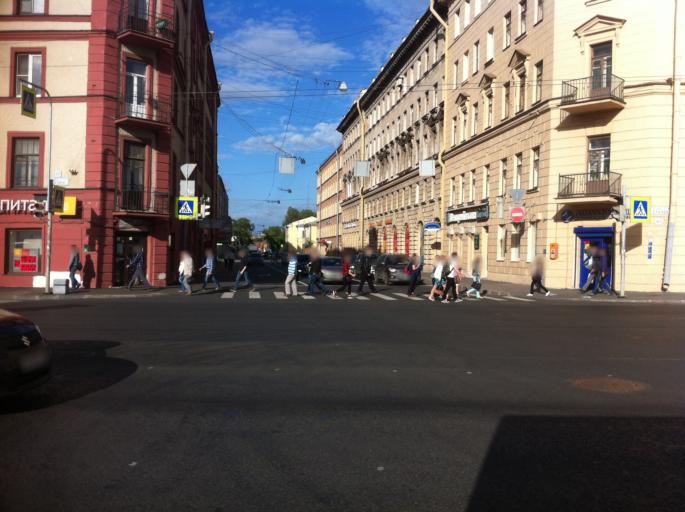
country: RU
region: St.-Petersburg
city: Admiralteisky
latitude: 59.8994
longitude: 30.2748
